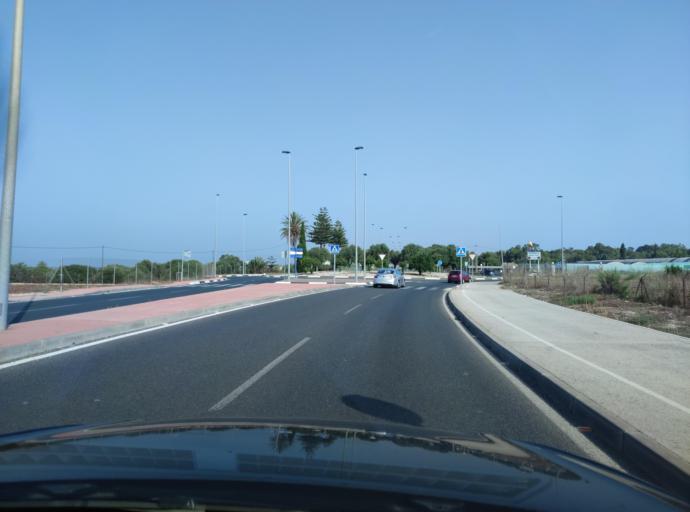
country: ES
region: Valencia
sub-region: Provincia de Alicante
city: Santa Pola
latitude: 38.2048
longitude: -0.5791
